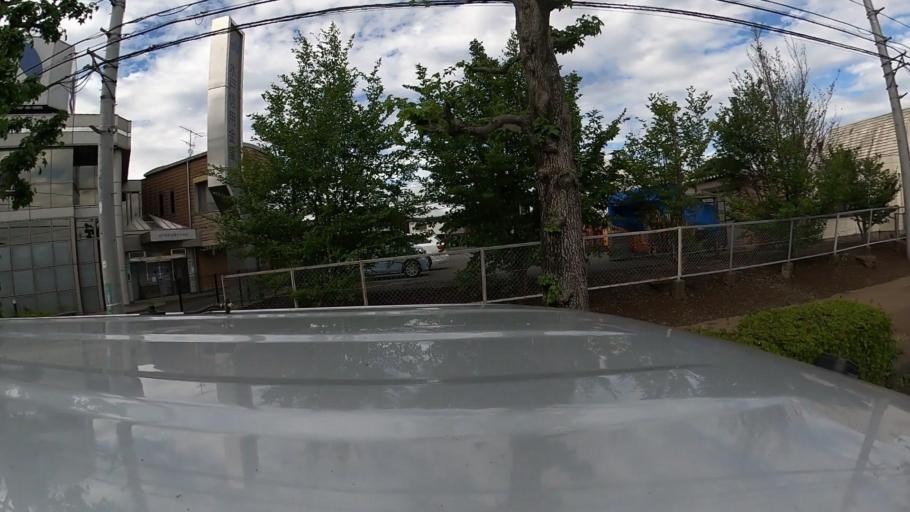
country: JP
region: Ibaraki
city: Ushiku
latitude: 35.9856
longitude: 140.1562
